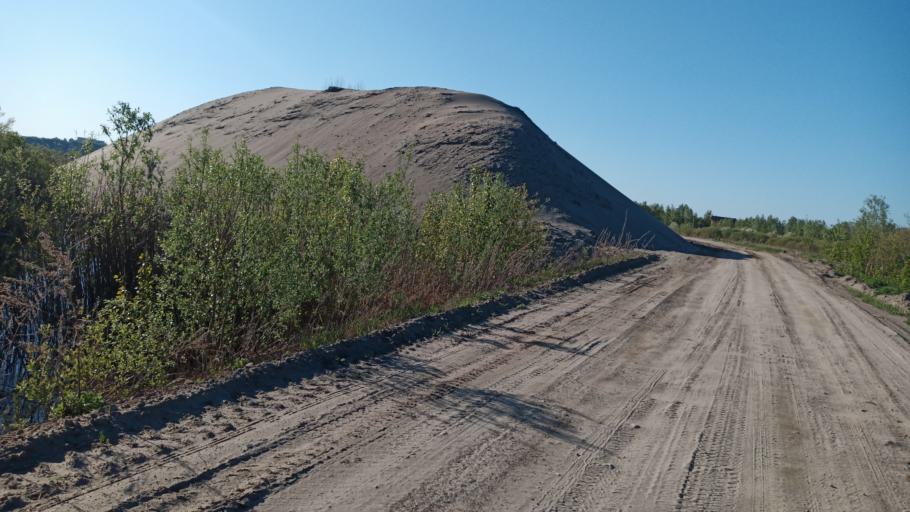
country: RU
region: Altai Krai
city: Zaton
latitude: 53.3090
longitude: 83.8235
